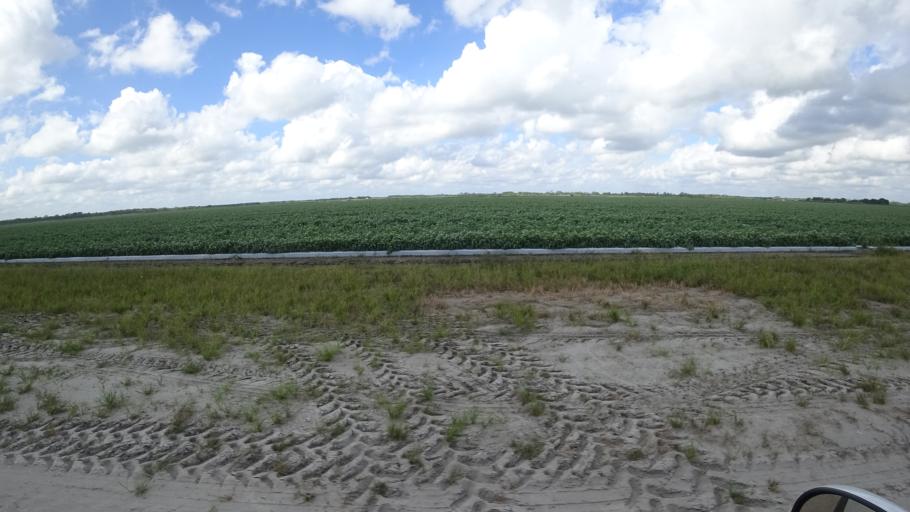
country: US
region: Florida
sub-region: Sarasota County
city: Lake Sarasota
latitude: 27.4090
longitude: -82.1998
